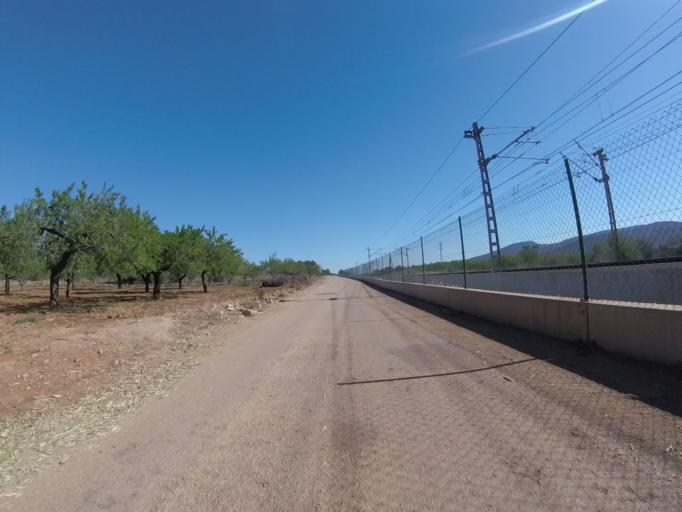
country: ES
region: Valencia
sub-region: Provincia de Castello
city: Alcala de Xivert
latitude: 40.3304
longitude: 0.2477
